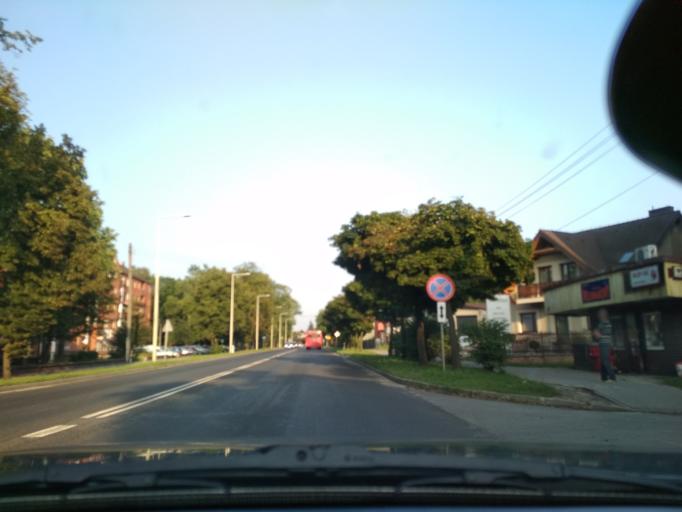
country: PL
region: Silesian Voivodeship
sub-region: Powiat zawiercianski
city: Zawiercie
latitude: 50.4799
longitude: 19.4425
